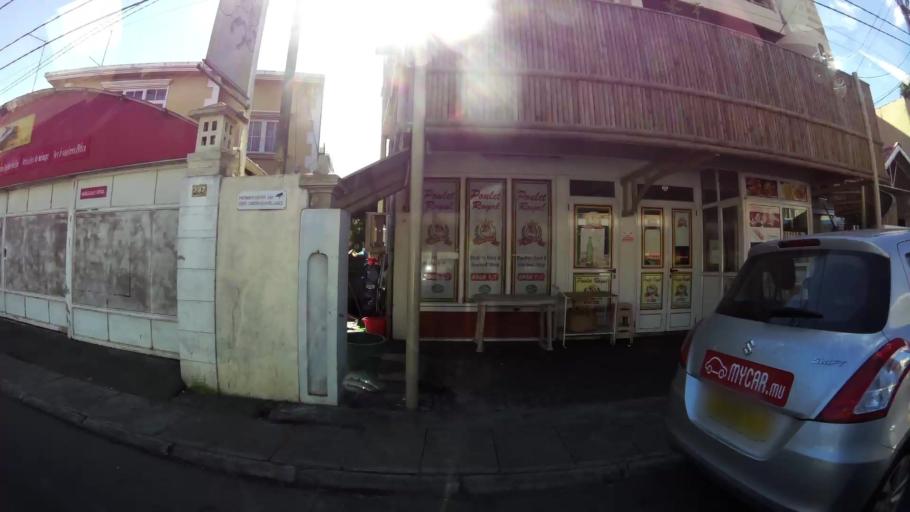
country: MU
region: Plaines Wilhems
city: Quatre Bornes
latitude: -20.2769
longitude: 57.4627
